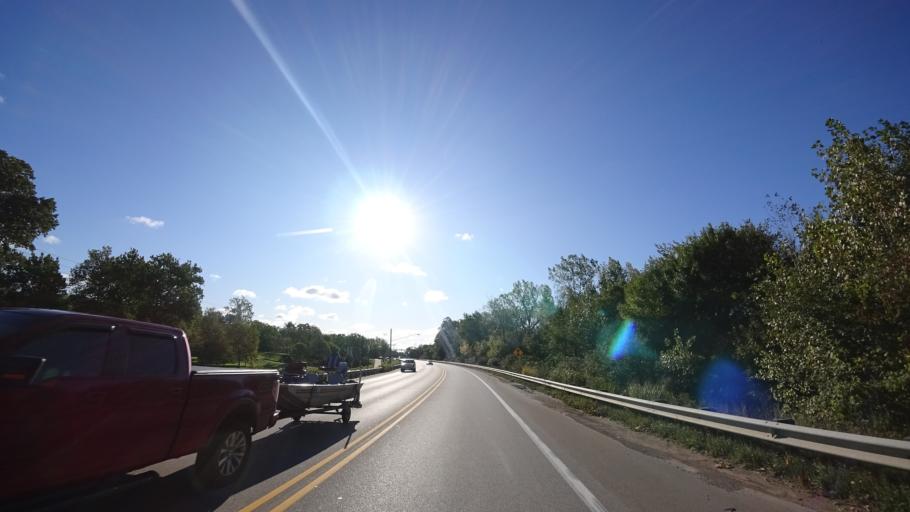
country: US
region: Michigan
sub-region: Kent County
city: Grandville
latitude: 42.9169
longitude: -85.7709
